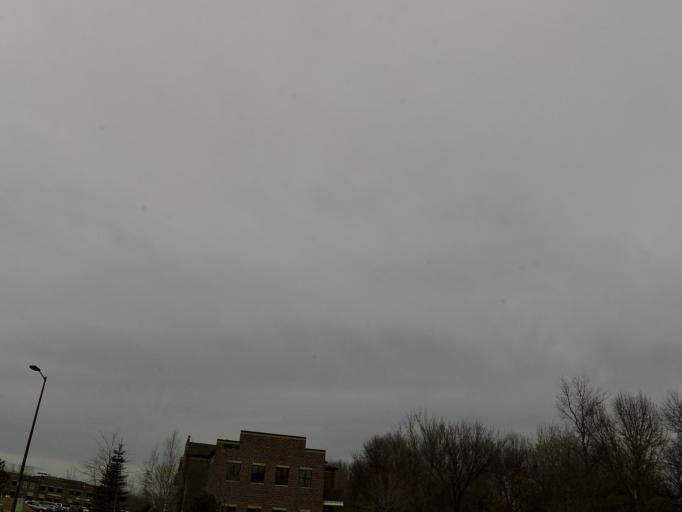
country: US
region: Minnesota
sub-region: Scott County
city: Savage
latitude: 44.7718
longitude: -93.3857
